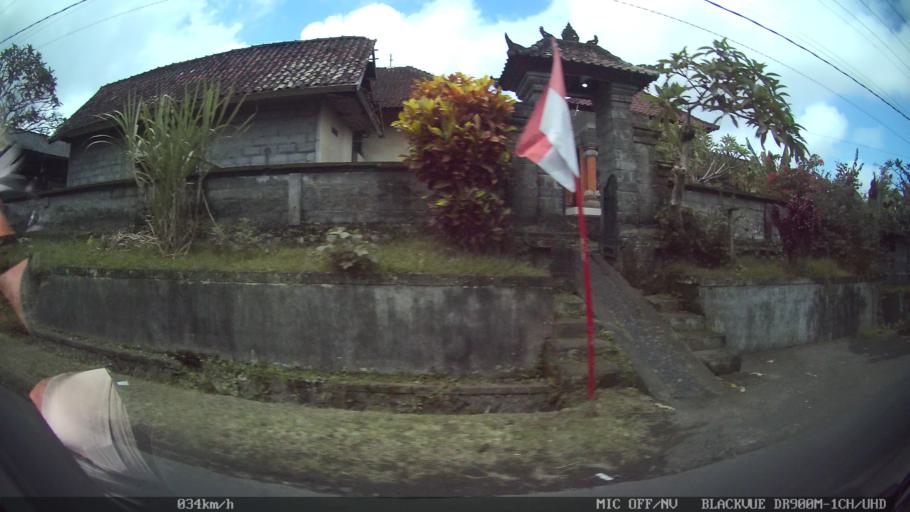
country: ID
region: Bali
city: Banjar Abuan
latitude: -8.4554
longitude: 115.3408
